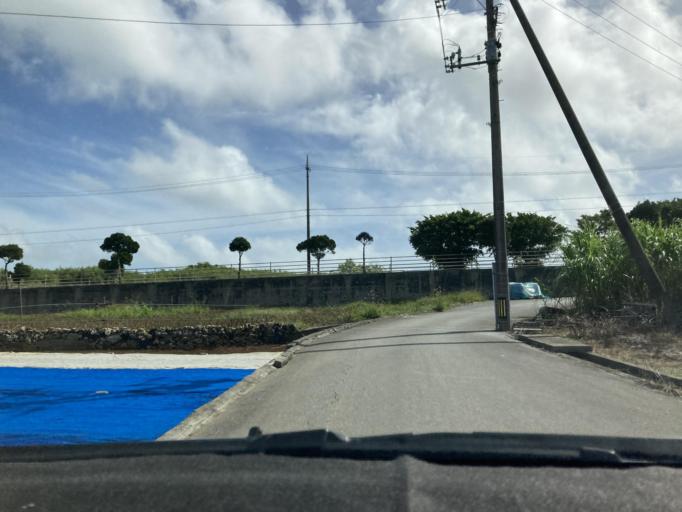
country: JP
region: Okinawa
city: Itoman
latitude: 26.0975
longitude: 127.6651
